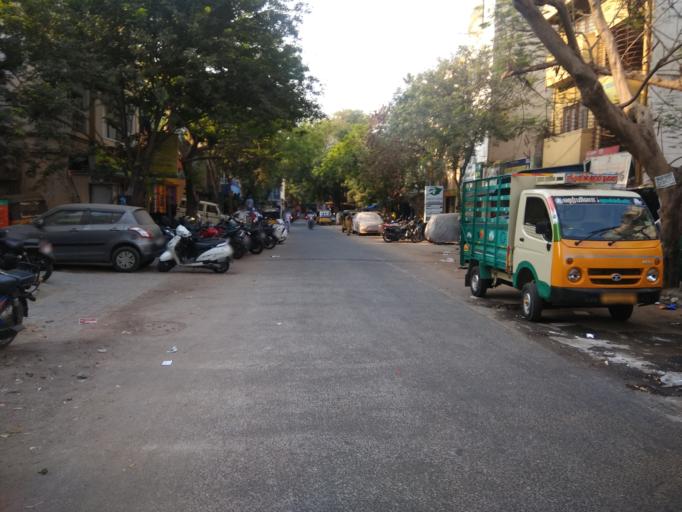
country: IN
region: Tamil Nadu
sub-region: Kancheepuram
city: Alandur
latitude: 13.0241
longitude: 80.2272
